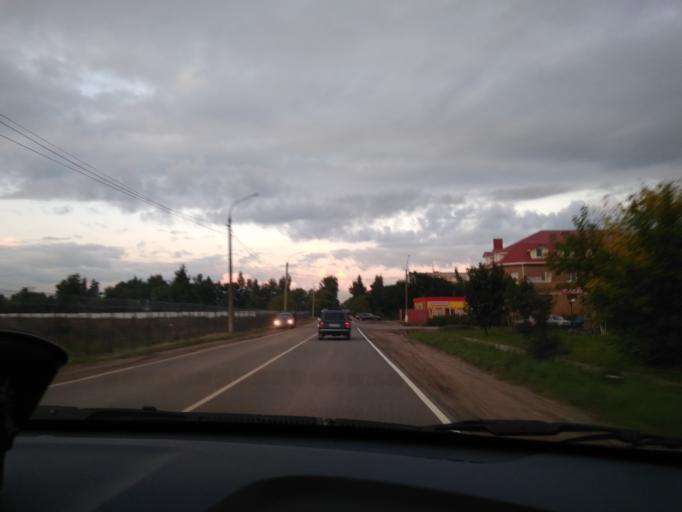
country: RU
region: Moskovskaya
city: Ramenskoye
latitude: 55.4932
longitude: 38.1683
